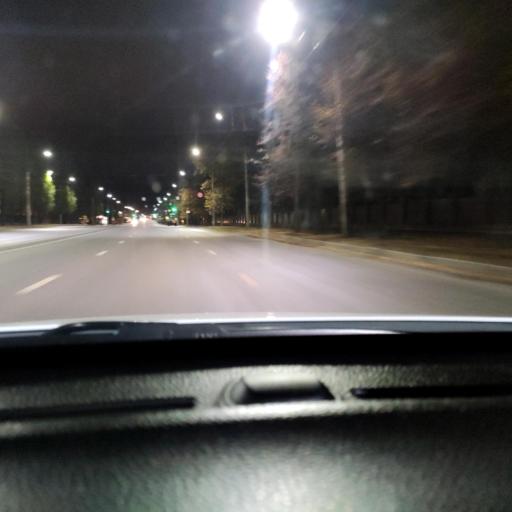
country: RU
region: Voronezj
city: Voronezh
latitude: 51.6777
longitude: 39.2588
